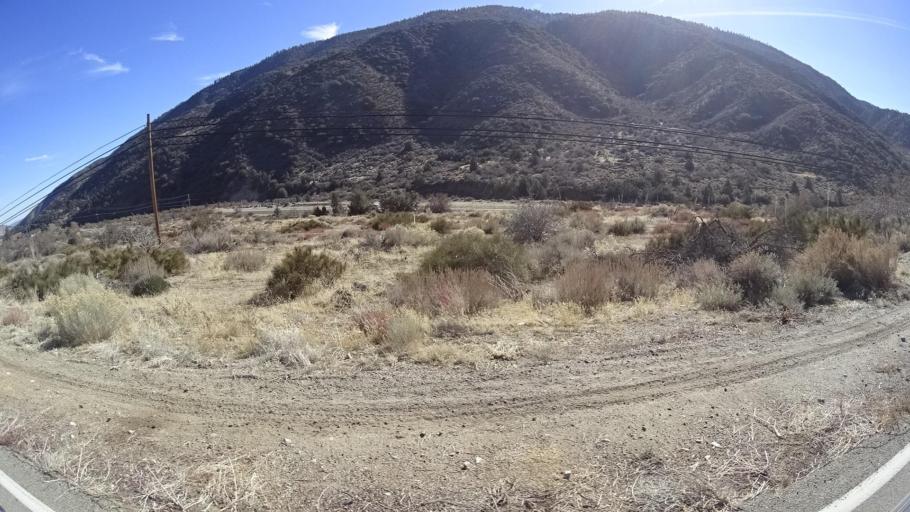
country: US
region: California
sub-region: Kern County
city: Frazier Park
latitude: 34.8222
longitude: -118.9665
